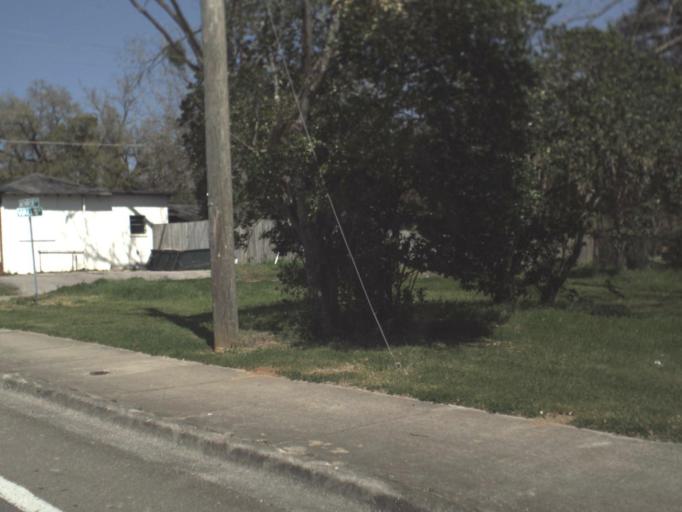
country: US
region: Florida
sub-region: Leon County
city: Tallahassee
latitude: 30.4180
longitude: -84.2806
